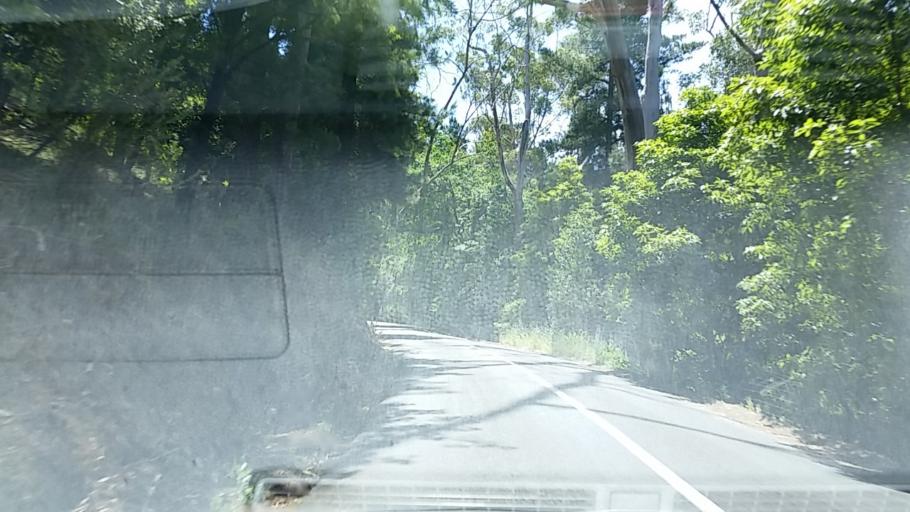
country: AU
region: South Australia
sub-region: Adelaide Hills
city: Upper Sturt
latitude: -35.0234
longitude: 138.6865
